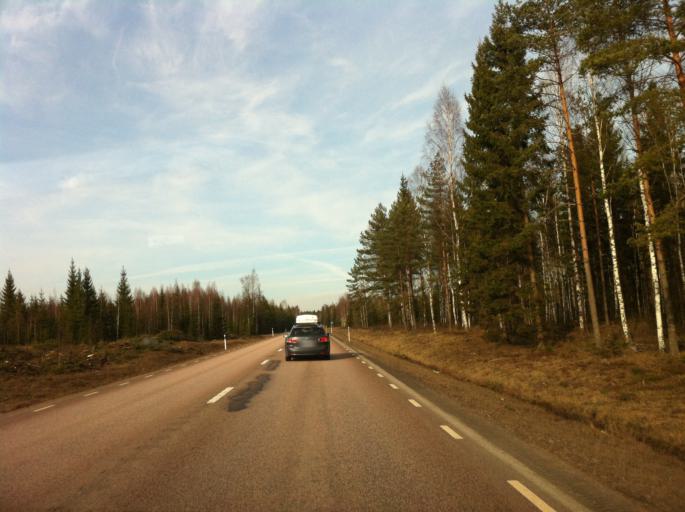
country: SE
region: Vaermland
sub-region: Kristinehamns Kommun
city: Bjorneborg
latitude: 59.1840
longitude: 14.1790
